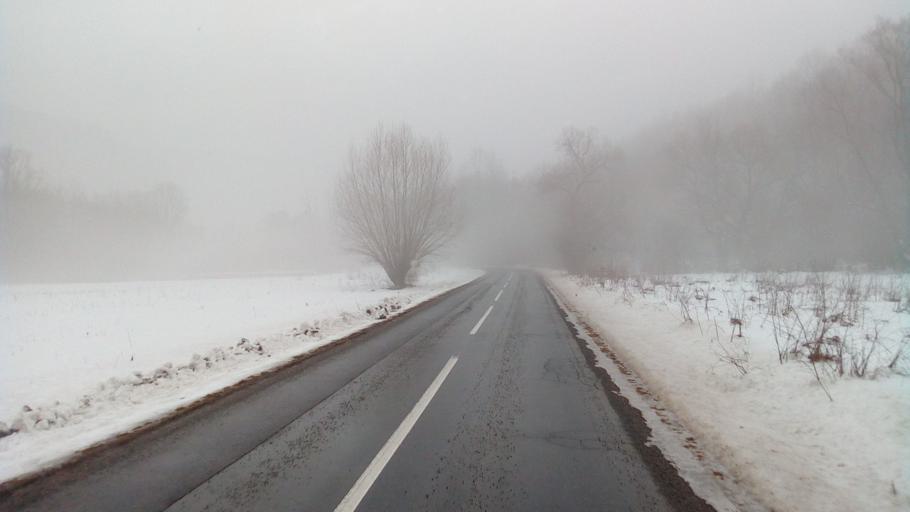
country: HR
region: Sisacko-Moslavacka
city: Petrinja
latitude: 45.3712
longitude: 16.2810
